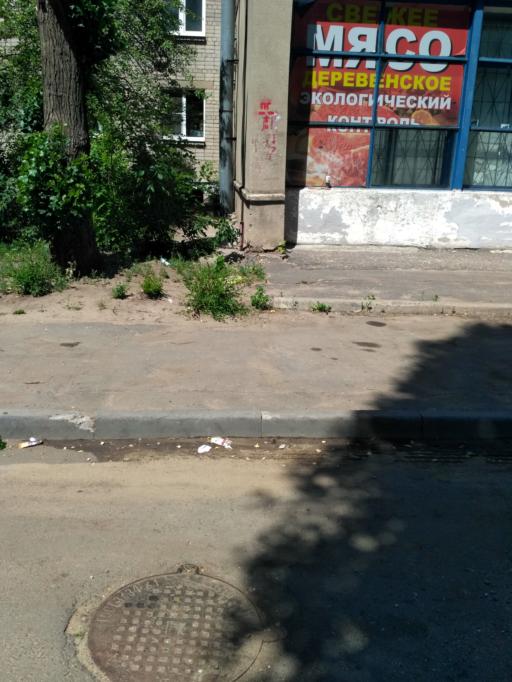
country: RU
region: Voronezj
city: Voronezh
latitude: 51.6555
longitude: 39.1333
